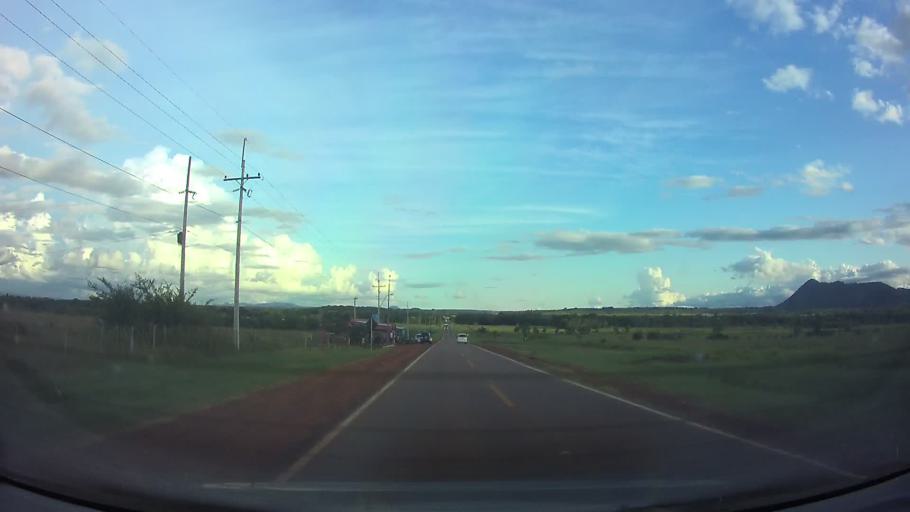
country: PY
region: Paraguari
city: Carapegua
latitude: -25.8289
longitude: -57.1592
